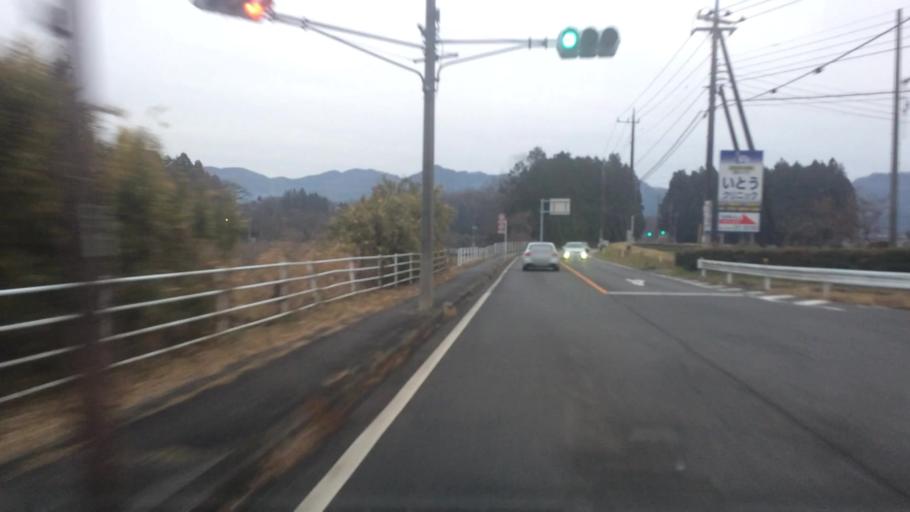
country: JP
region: Tochigi
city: Imaichi
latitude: 36.6699
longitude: 139.7744
